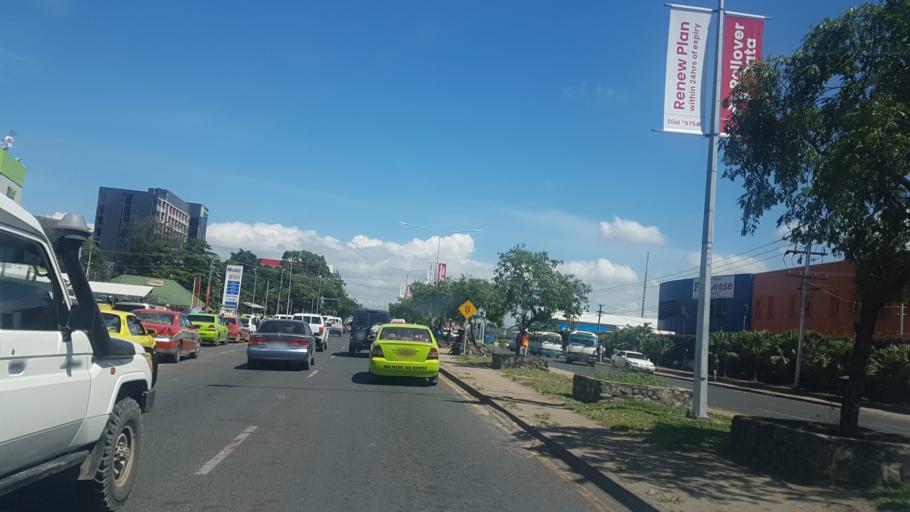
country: PG
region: National Capital
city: Port Moresby
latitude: -9.4473
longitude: 147.1839
